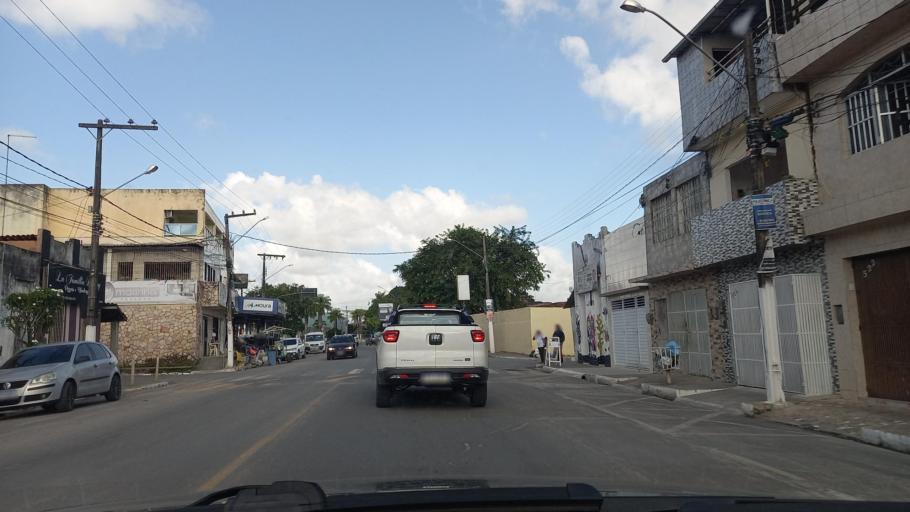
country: BR
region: Pernambuco
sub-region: Goiana
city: Goiana
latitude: -7.5608
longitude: -34.9929
